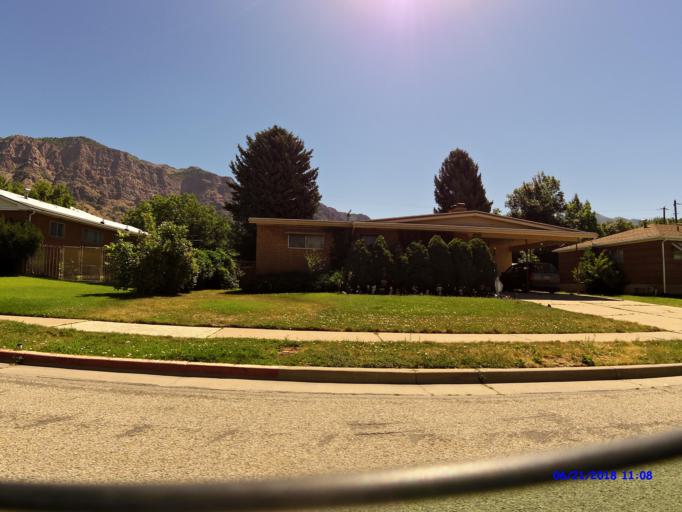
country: US
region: Utah
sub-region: Weber County
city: Ogden
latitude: 41.2553
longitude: -111.9551
